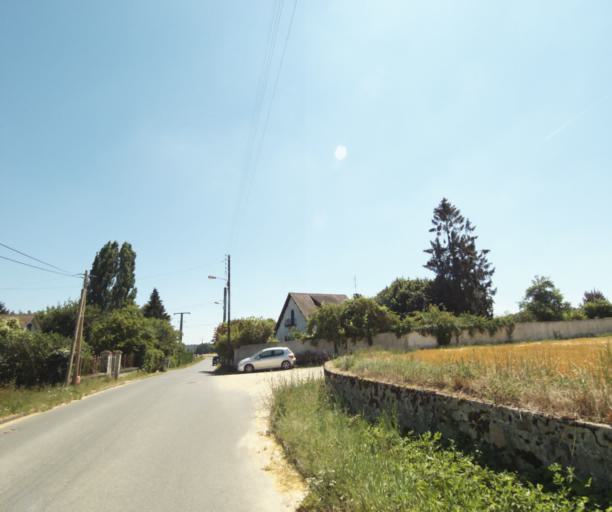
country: FR
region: Ile-de-France
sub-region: Departement de Seine-et-Marne
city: Noisy-sur-Ecole
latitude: 48.3651
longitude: 2.5093
